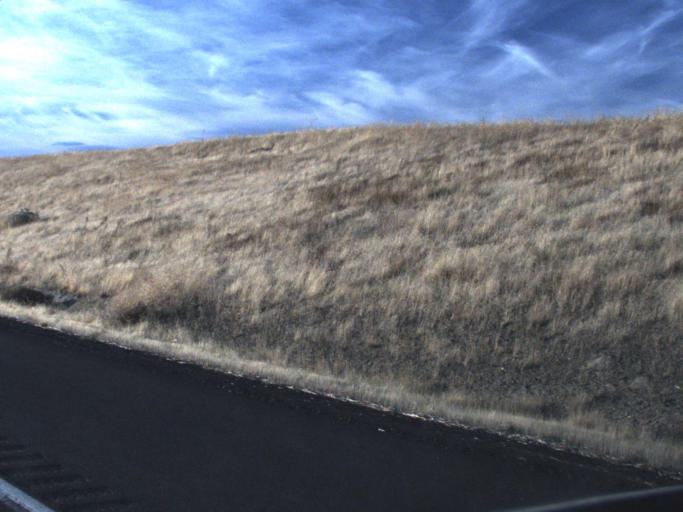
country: US
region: Washington
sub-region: Walla Walla County
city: Garrett
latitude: 46.0514
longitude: -118.5032
